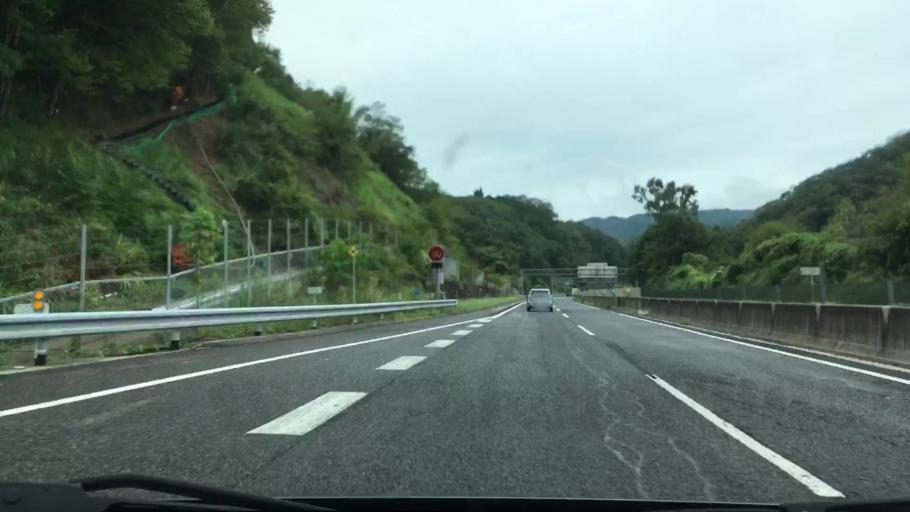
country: JP
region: Hyogo
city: Yamazakicho-nakabirose
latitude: 35.0202
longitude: 134.3826
